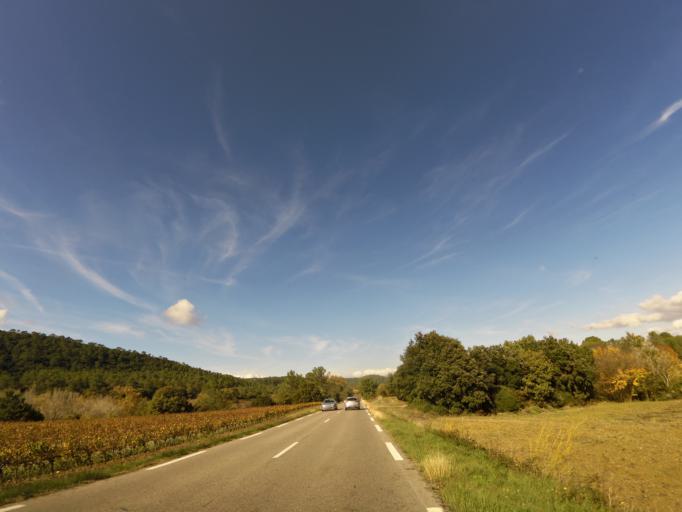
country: FR
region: Languedoc-Roussillon
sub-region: Departement du Gard
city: Ledignan
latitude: 43.9158
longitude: 4.1089
